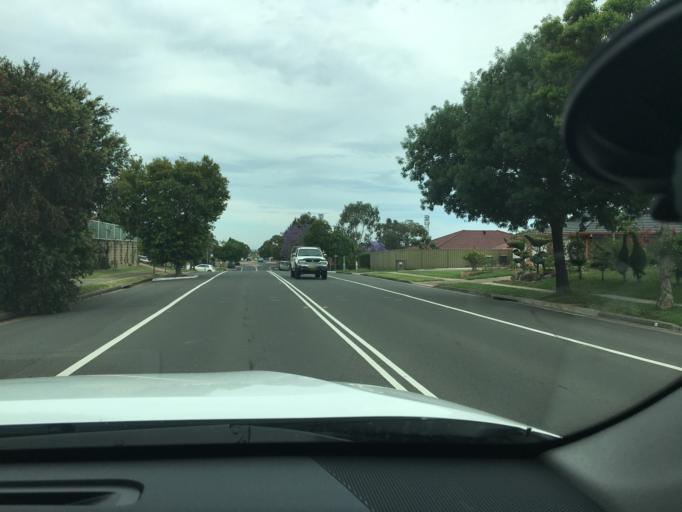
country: AU
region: New South Wales
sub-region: Fairfield
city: Horsley Park
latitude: -33.8621
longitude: 150.8755
